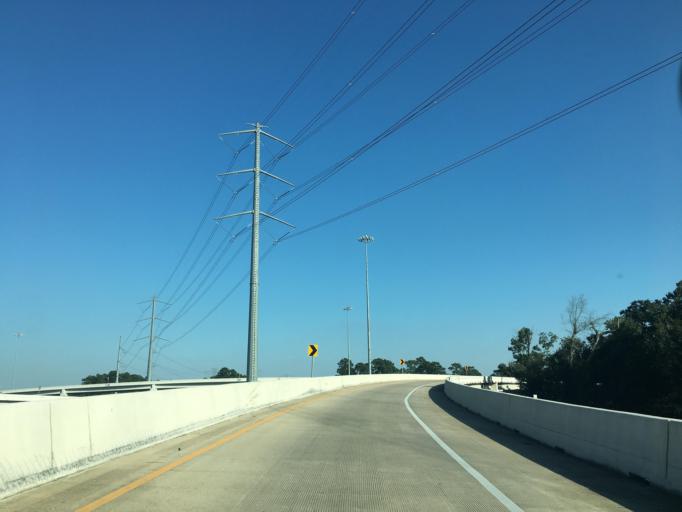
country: US
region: Texas
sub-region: Harris County
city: Spring
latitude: 30.0928
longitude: -95.4160
